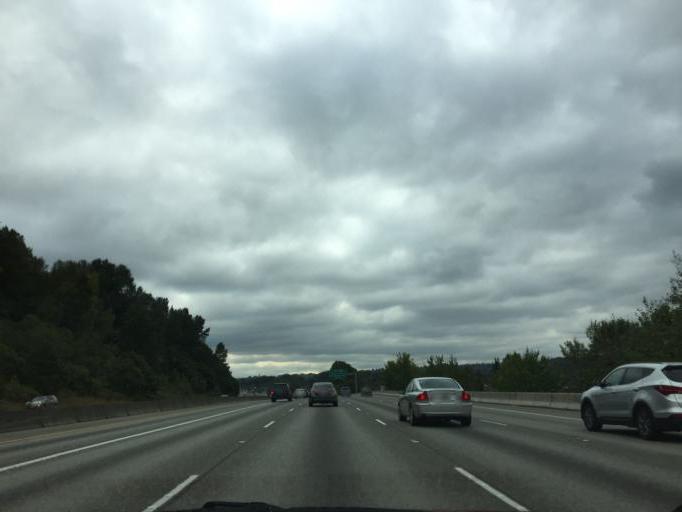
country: US
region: Washington
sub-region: King County
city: Riverton
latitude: 47.5188
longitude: -122.2896
